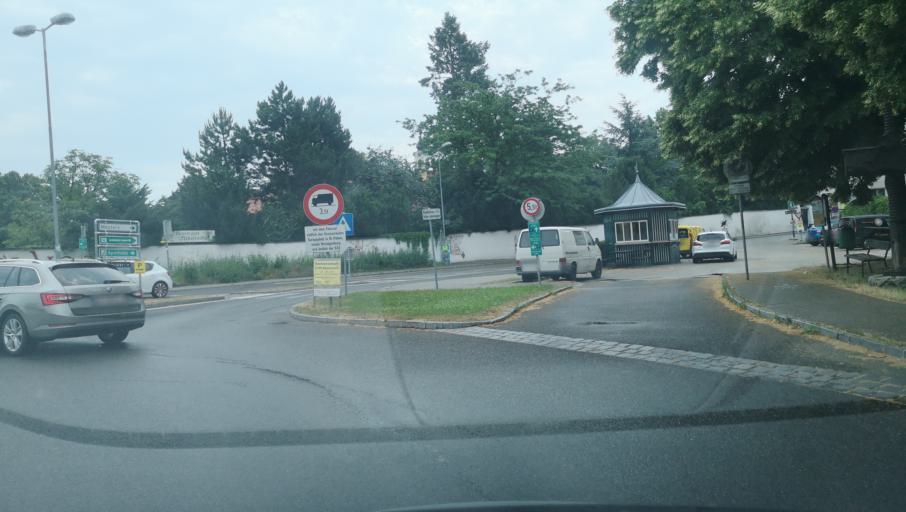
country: AT
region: Lower Austria
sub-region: Politischer Bezirk Krems
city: Weinzierl bei Krems
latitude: 48.3952
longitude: 15.5763
